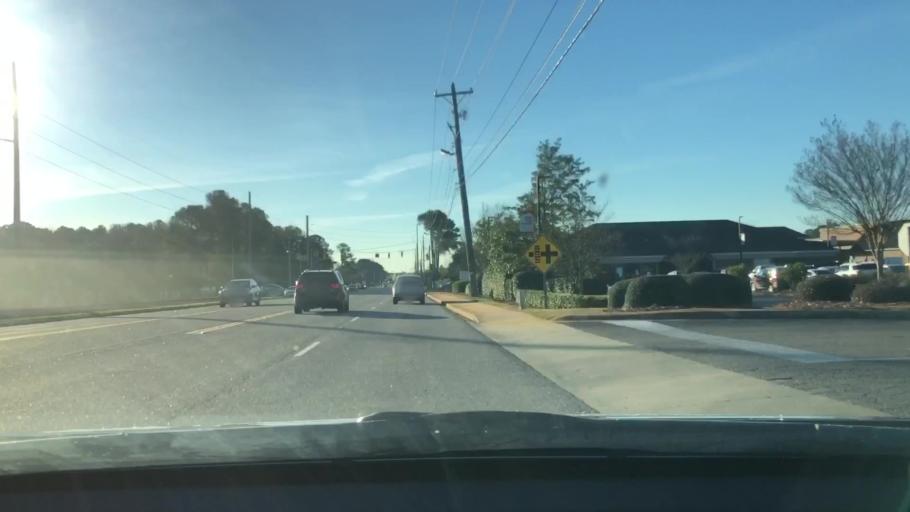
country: US
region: South Carolina
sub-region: Lexington County
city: Irmo
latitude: 34.0793
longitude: -81.1798
